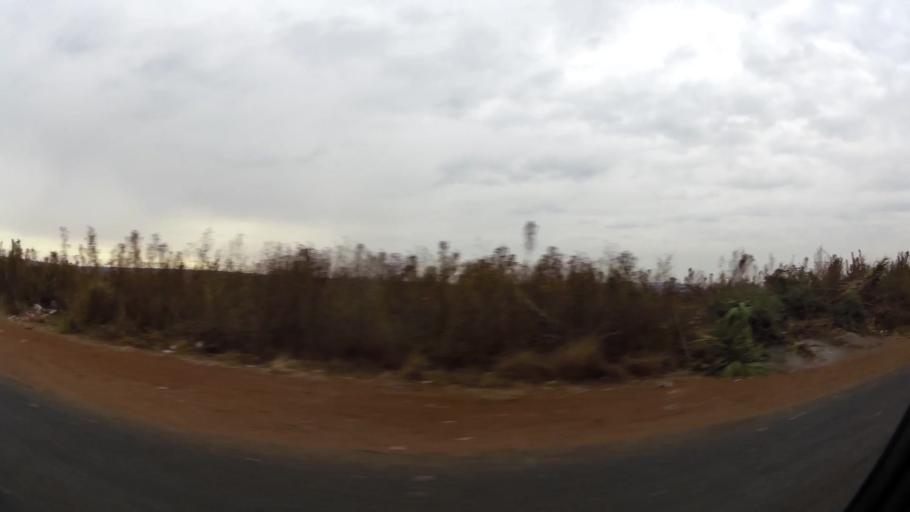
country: ZA
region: Gauteng
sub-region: City of Johannesburg Metropolitan Municipality
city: Roodepoort
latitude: -26.1654
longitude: 27.8064
